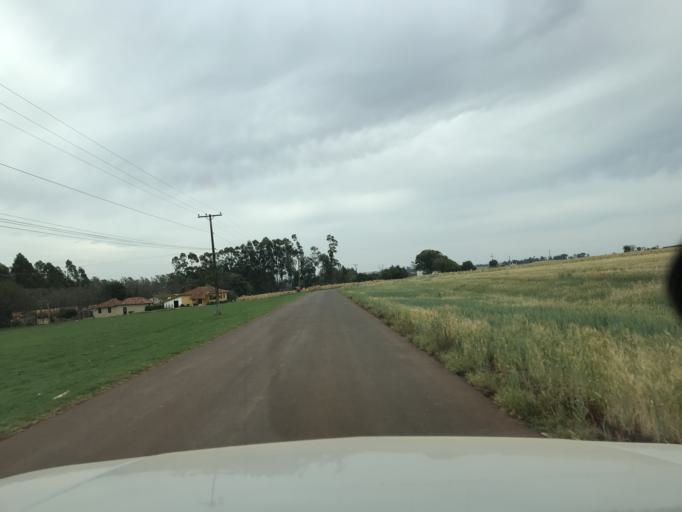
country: BR
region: Parana
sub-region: Marechal Candido Rondon
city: Marechal Candido Rondon
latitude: -24.4630
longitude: -53.9654
